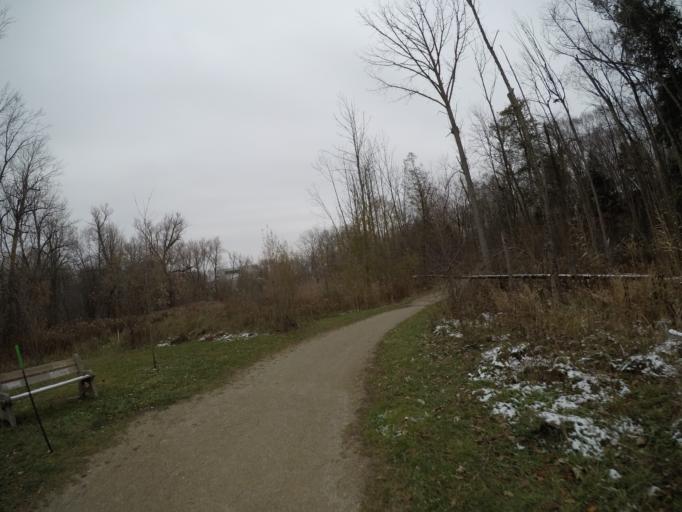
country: CA
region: Ontario
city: Waterloo
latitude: 43.4871
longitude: -80.5110
